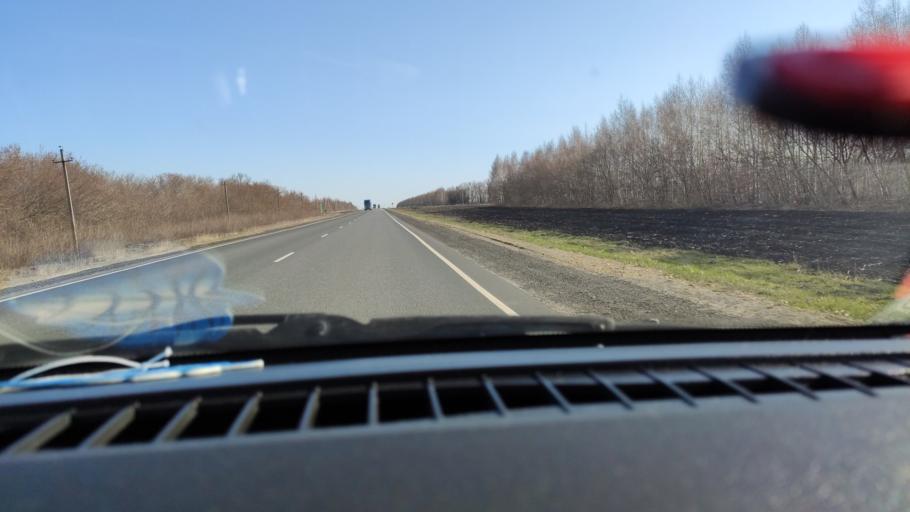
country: RU
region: Samara
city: Syzran'
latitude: 52.9839
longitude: 48.3157
